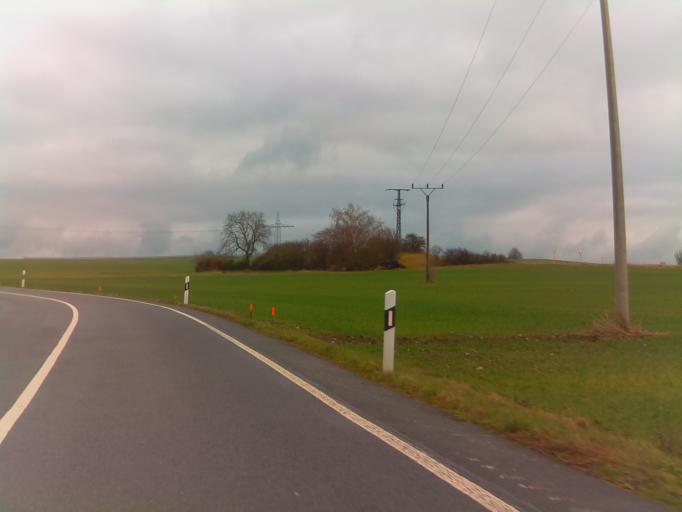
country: DE
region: Thuringia
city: Bucha
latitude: 50.8549
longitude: 11.4998
